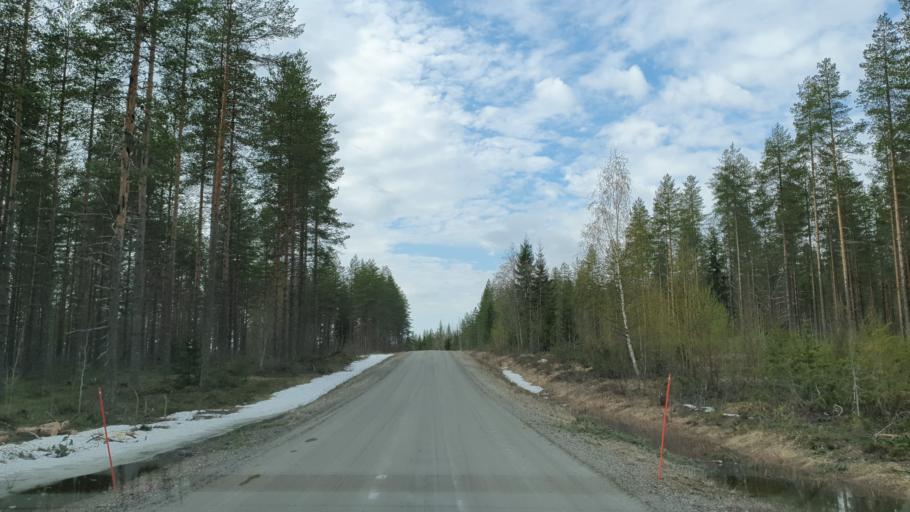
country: FI
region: Kainuu
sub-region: Kehys-Kainuu
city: Kuhmo
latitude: 64.0975
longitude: 29.9230
